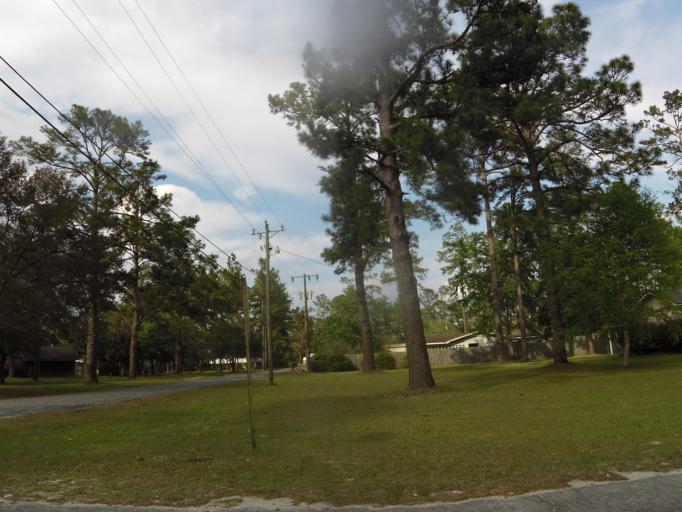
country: US
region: Georgia
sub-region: Charlton County
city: Folkston
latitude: 30.8344
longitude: -81.9861
